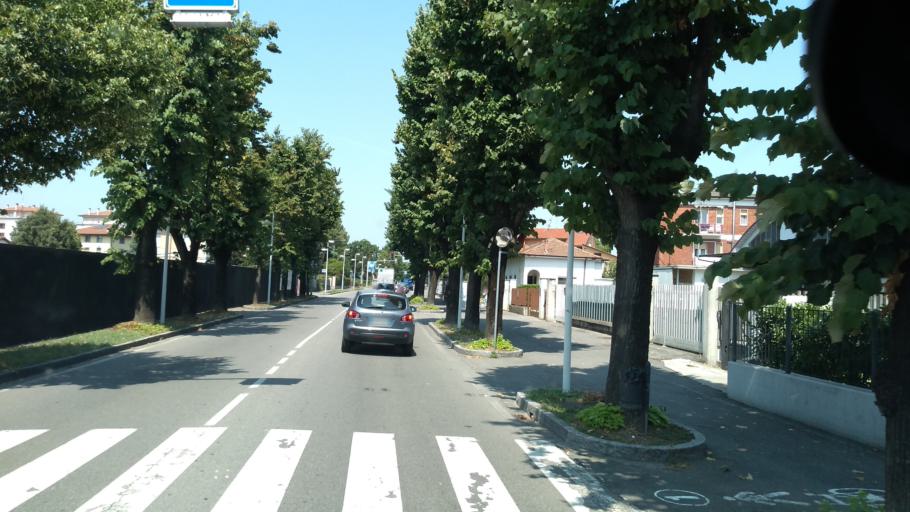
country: IT
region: Lombardy
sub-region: Provincia di Bergamo
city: Treviglio
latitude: 45.5175
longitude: 9.5860
